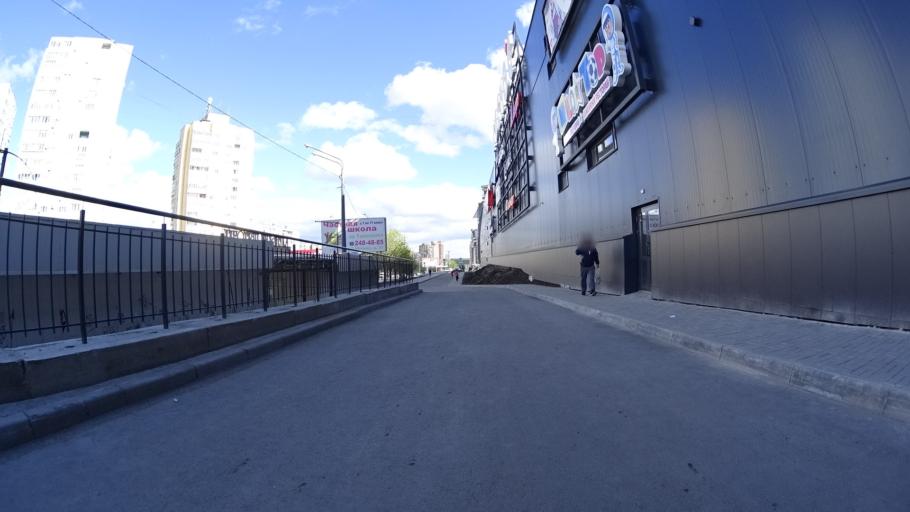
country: RU
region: Chelyabinsk
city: Roshchino
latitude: 55.1816
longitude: 61.2930
